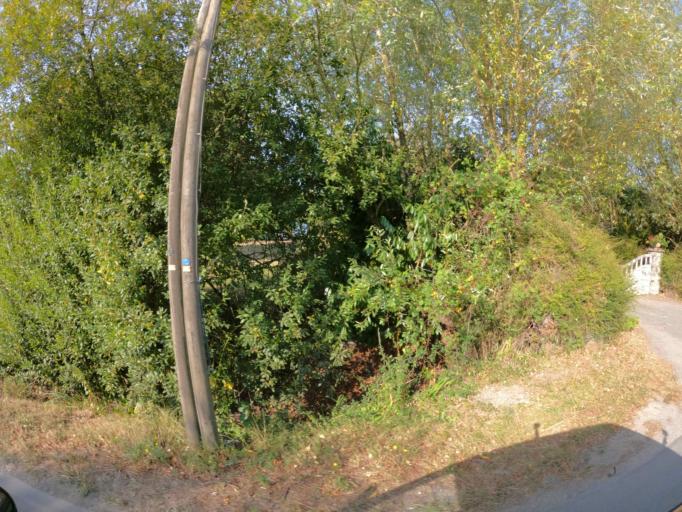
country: FR
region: Pays de la Loire
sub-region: Departement de la Vendee
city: Le Perrier
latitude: 46.8098
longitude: -1.9886
